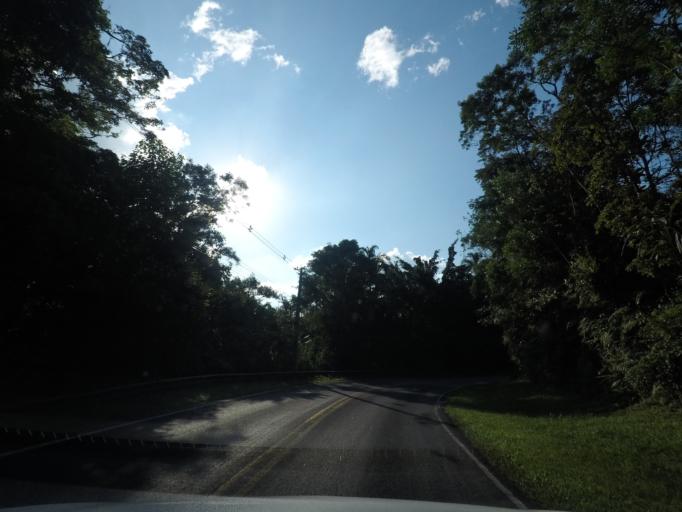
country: BR
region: Parana
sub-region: Antonina
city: Antonina
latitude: -25.4266
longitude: -48.8764
